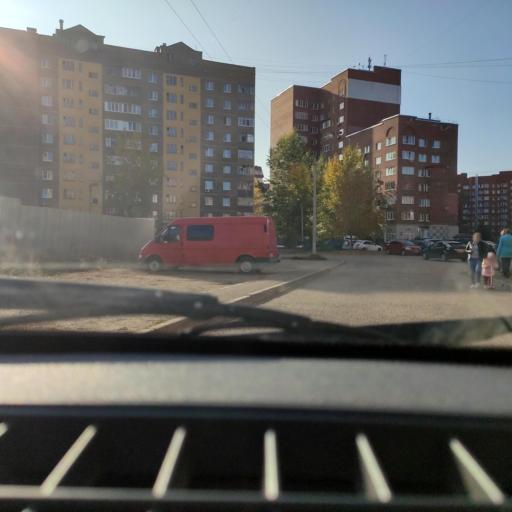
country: RU
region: Bashkortostan
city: Ufa
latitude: 54.7754
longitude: 56.0722
